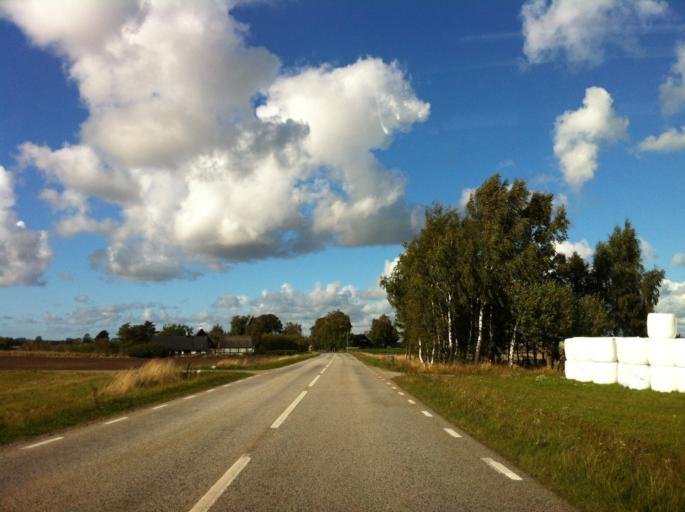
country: SE
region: Skane
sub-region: Kavlinge Kommun
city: Hofterup
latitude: 55.8438
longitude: 13.0100
